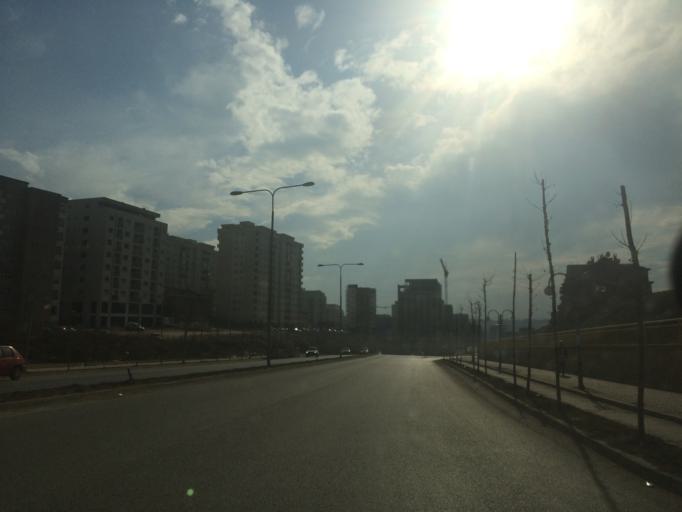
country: XK
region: Pristina
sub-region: Komuna e Prishtines
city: Pristina
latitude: 42.6519
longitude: 21.1754
